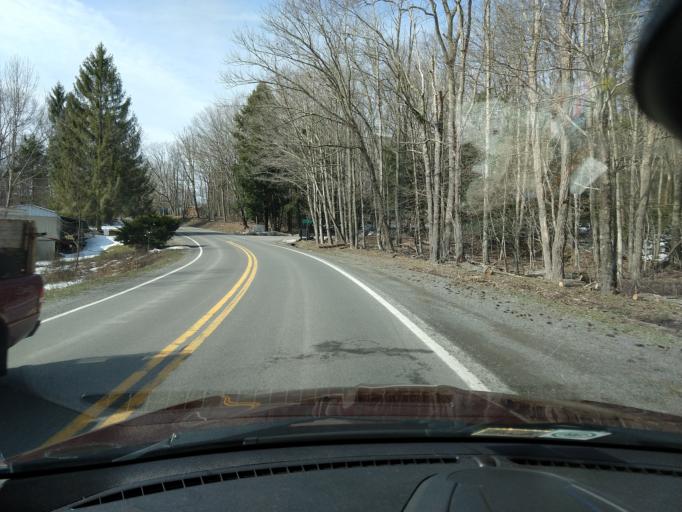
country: US
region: West Virginia
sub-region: Pocahontas County
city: Marlinton
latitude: 38.1091
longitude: -80.2711
